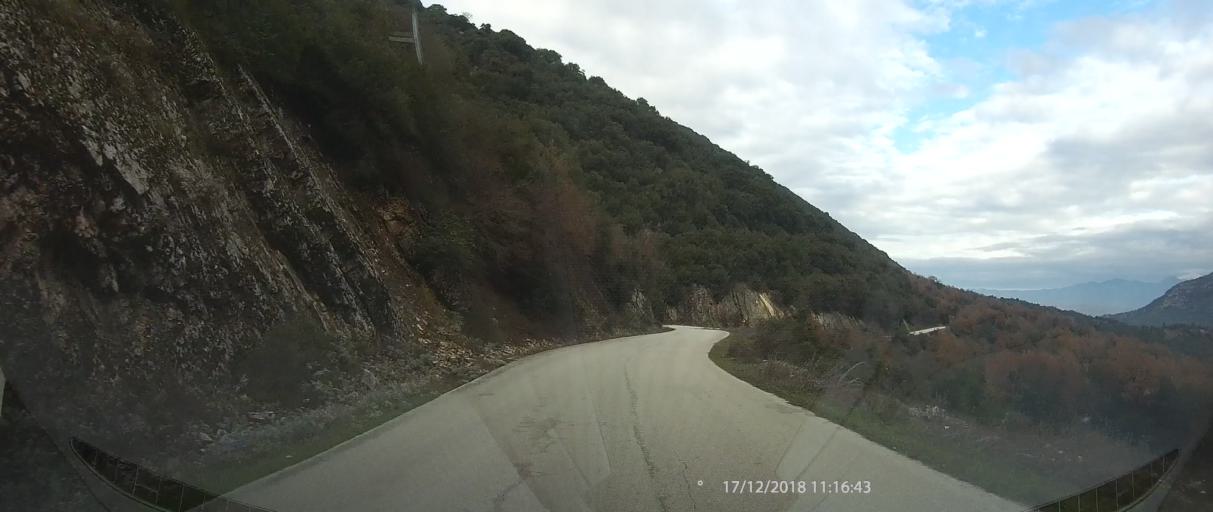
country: GR
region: Epirus
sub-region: Nomos Ioanninon
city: Kalpaki
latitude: 39.9375
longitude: 20.6654
